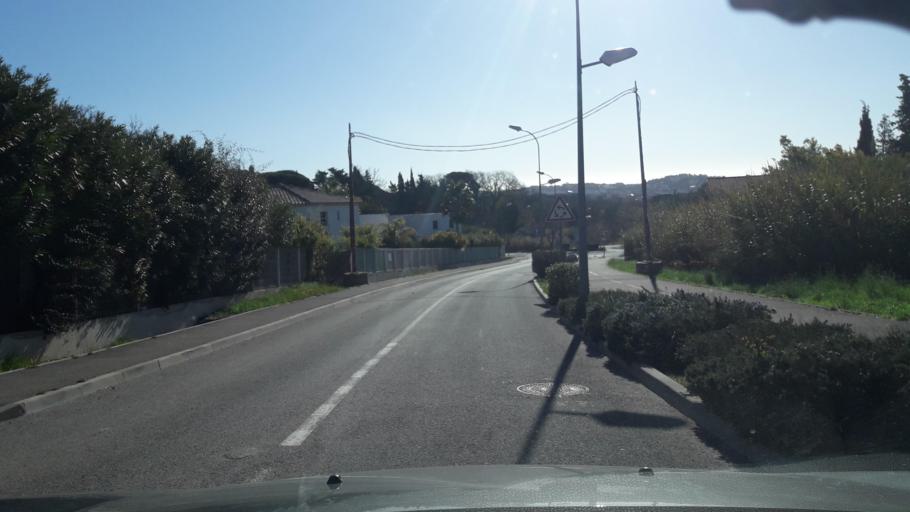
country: FR
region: Provence-Alpes-Cote d'Azur
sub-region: Departement du Var
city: Saint-Raphael
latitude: 43.4430
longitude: 6.7590
